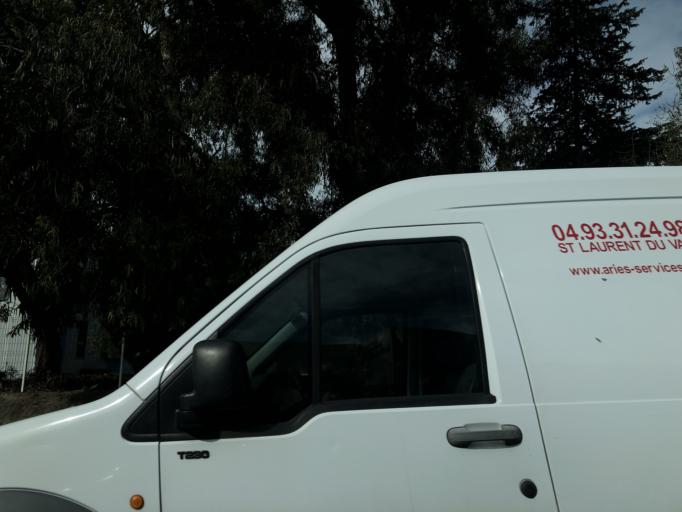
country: FR
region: Provence-Alpes-Cote d'Azur
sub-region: Departement des Alpes-Maritimes
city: Saint-Laurent-du-Var
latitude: 43.6888
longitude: 7.1863
